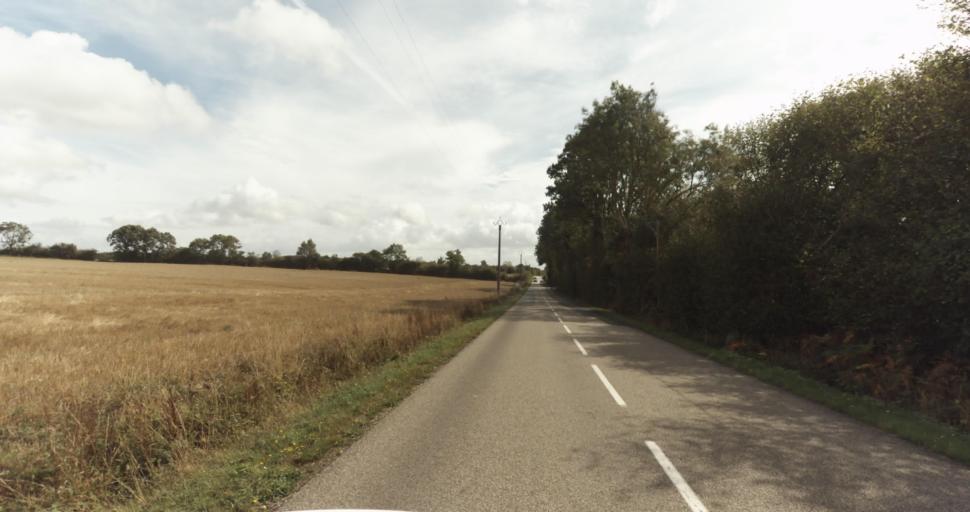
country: FR
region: Lower Normandy
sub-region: Departement de l'Orne
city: Sainte-Gauburge-Sainte-Colombe
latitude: 48.7992
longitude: 0.3984
